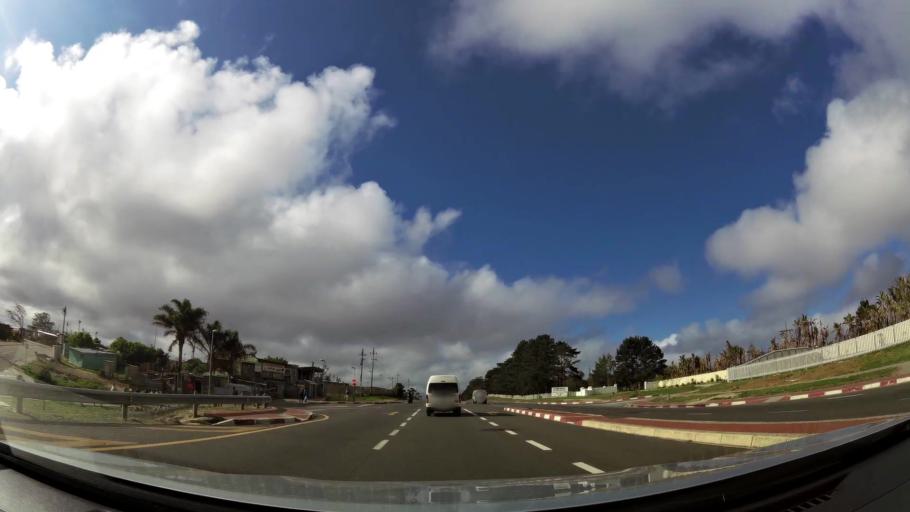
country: ZA
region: Western Cape
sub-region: Eden District Municipality
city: Plettenberg Bay
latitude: -34.0534
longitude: 23.3479
